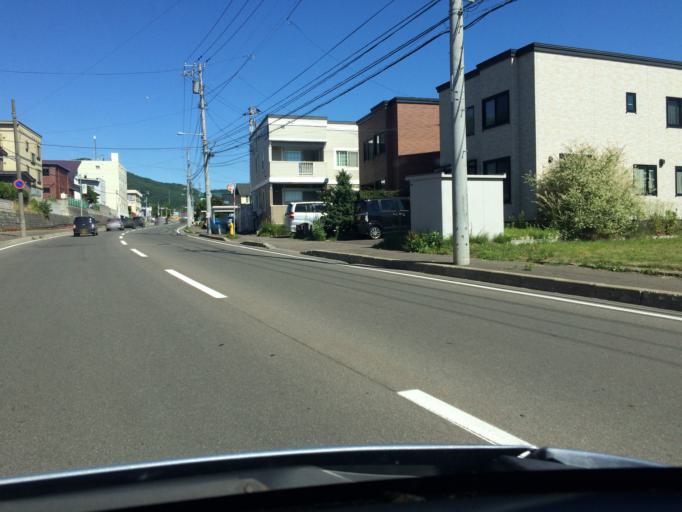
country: JP
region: Hokkaido
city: Sapporo
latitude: 43.0024
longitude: 141.3207
